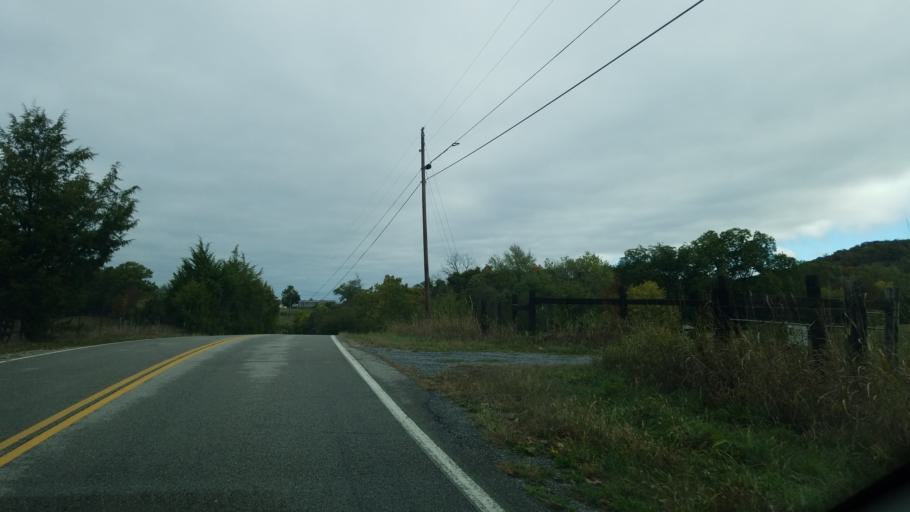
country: US
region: Tennessee
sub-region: Bradley County
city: Hopewell
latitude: 35.2692
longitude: -84.9707
